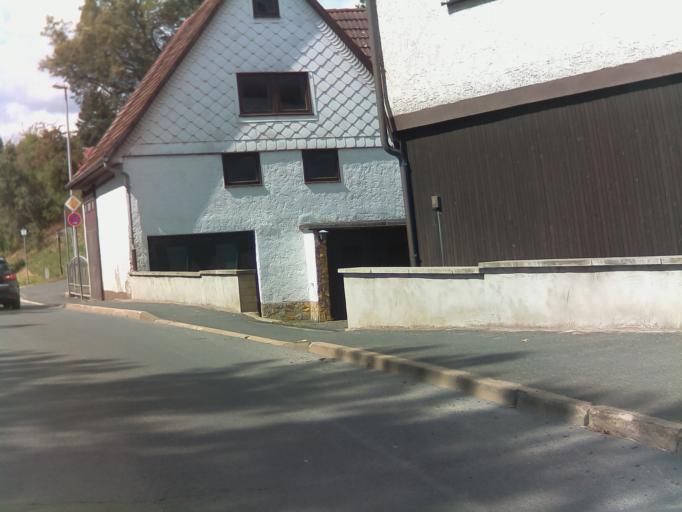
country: DE
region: Thuringia
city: Schmeheim
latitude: 50.6023
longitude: 10.5914
